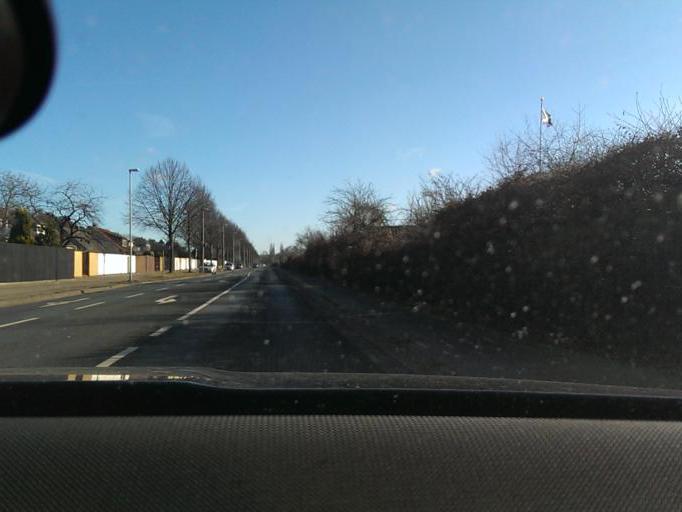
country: DE
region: Lower Saxony
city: Langenhagen
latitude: 52.4102
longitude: 9.7737
